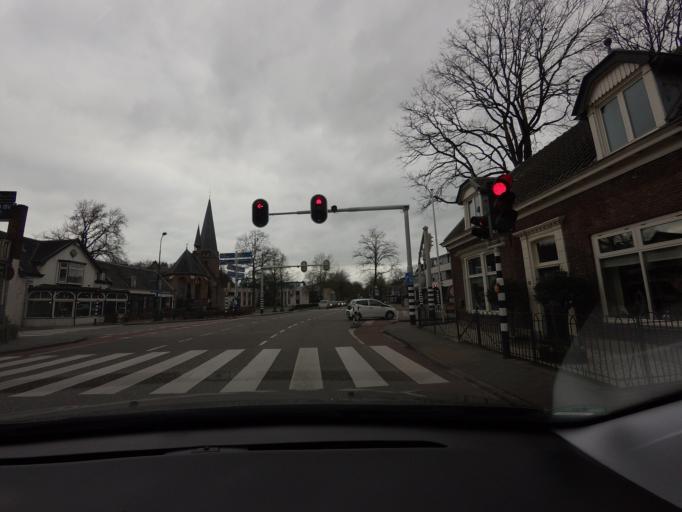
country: NL
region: Utrecht
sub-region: Gemeente Utrechtse Heuvelrug
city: Doorn
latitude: 52.0253
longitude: 5.3435
